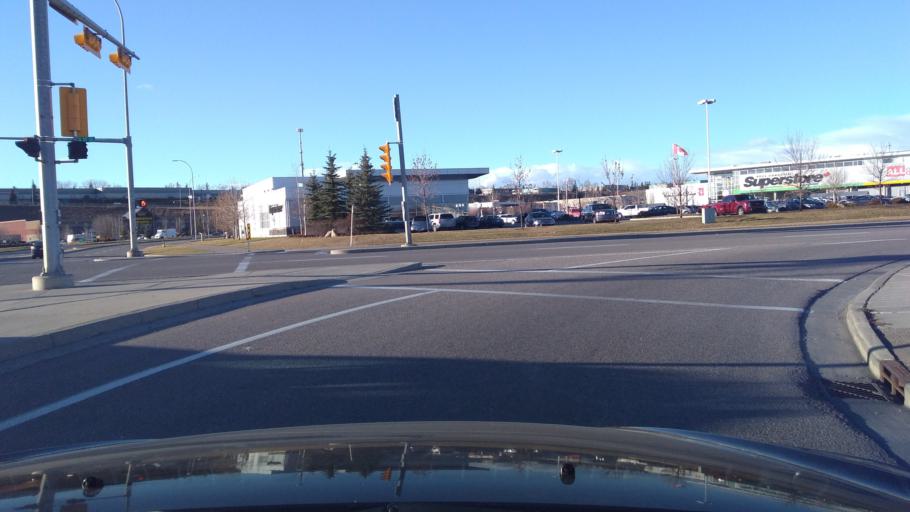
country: CA
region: Alberta
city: Calgary
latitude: 50.9842
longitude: -114.0414
